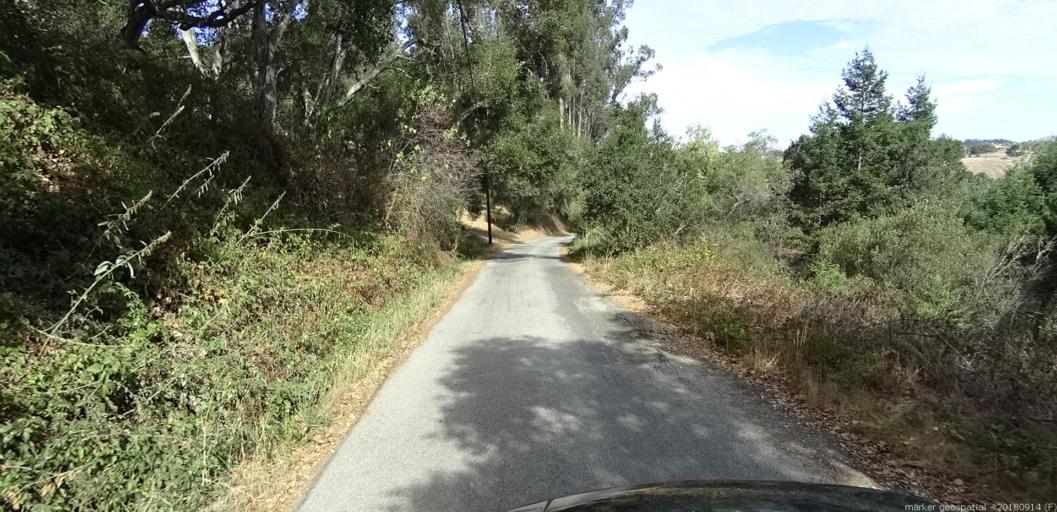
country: US
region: California
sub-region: San Benito County
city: Aromas
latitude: 36.8543
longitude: -121.6490
